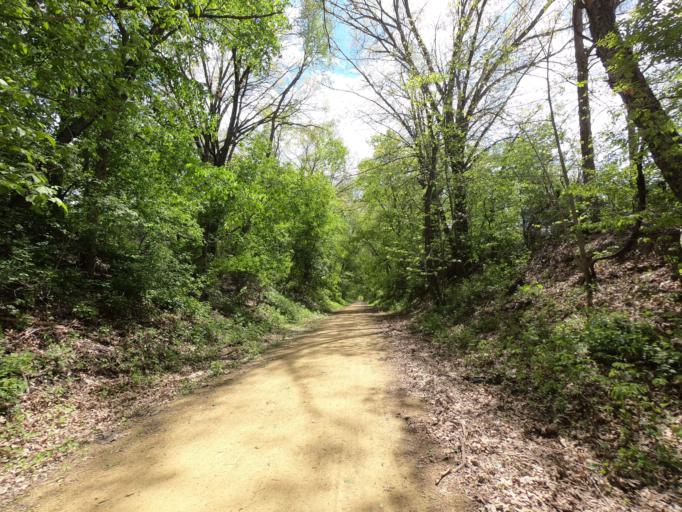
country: US
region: Wisconsin
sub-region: Dane County
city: Belleville
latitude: 42.9096
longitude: -89.5131
